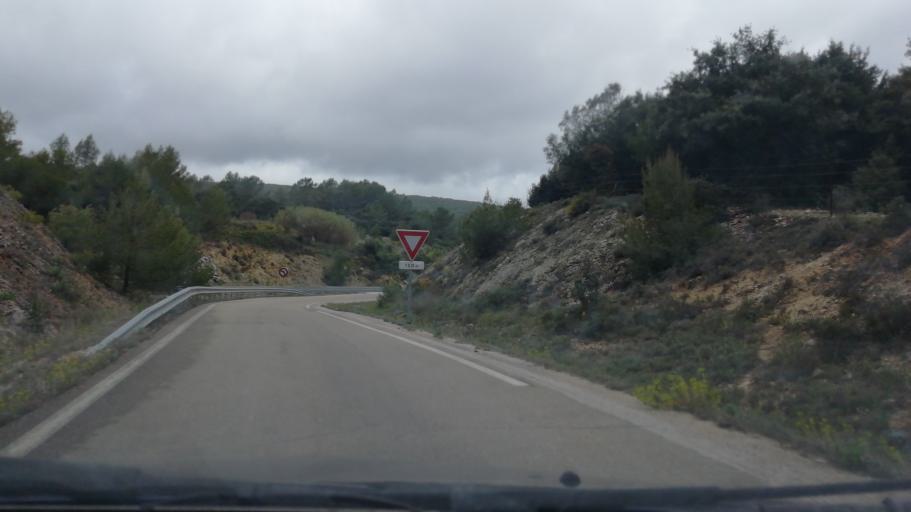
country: FR
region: Languedoc-Roussillon
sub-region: Departement de l'Herault
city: Saint-Gely-du-Fesc
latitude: 43.7108
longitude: 3.7992
